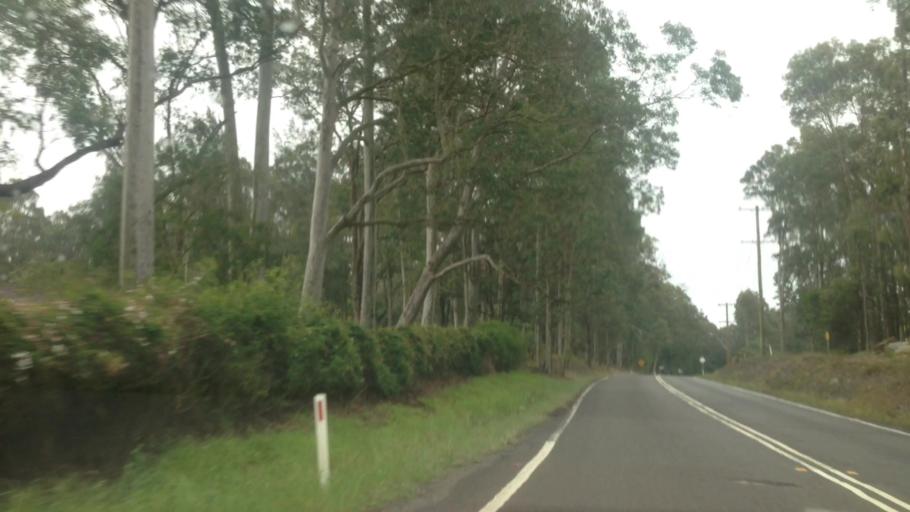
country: AU
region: New South Wales
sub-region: Wyong Shire
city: Little Jilliby
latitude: -33.2569
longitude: 151.3974
